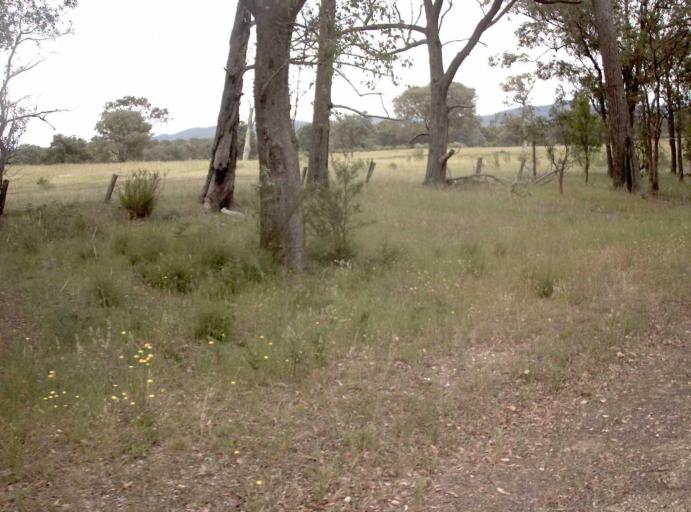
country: AU
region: Victoria
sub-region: East Gippsland
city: Bairnsdale
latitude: -37.7887
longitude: 147.3257
